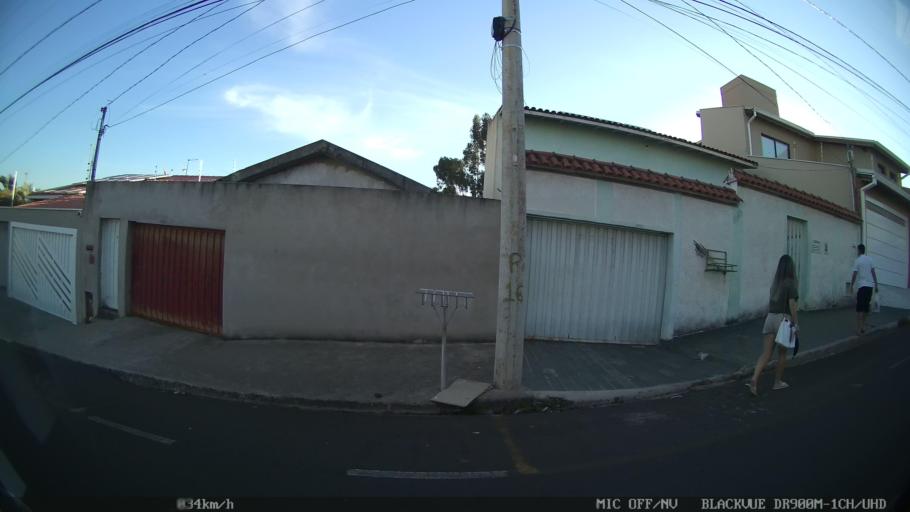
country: BR
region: Sao Paulo
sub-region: Franca
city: Franca
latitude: -20.5117
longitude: -47.3967
